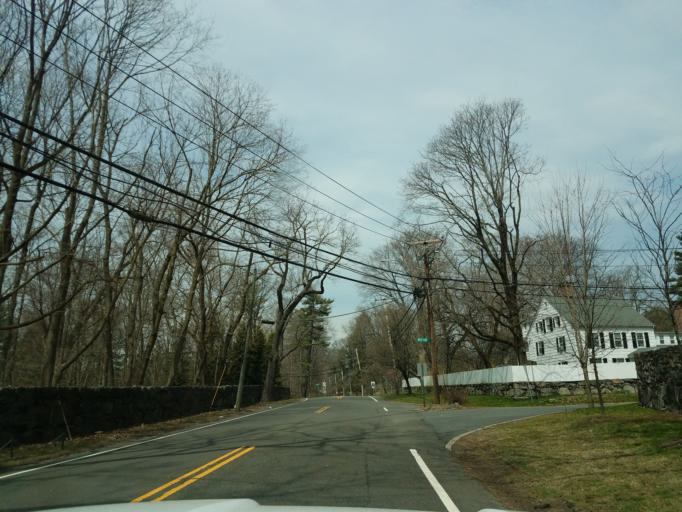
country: US
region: Connecticut
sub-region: Fairfield County
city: Greenwich
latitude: 41.0481
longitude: -73.6374
